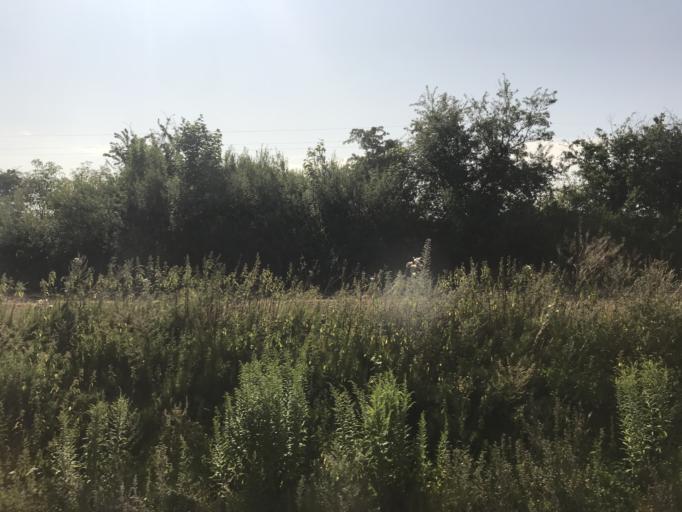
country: PL
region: Kujawsko-Pomorskie
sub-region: Powiat swiecki
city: Pruszcz
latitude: 53.3097
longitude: 18.1600
